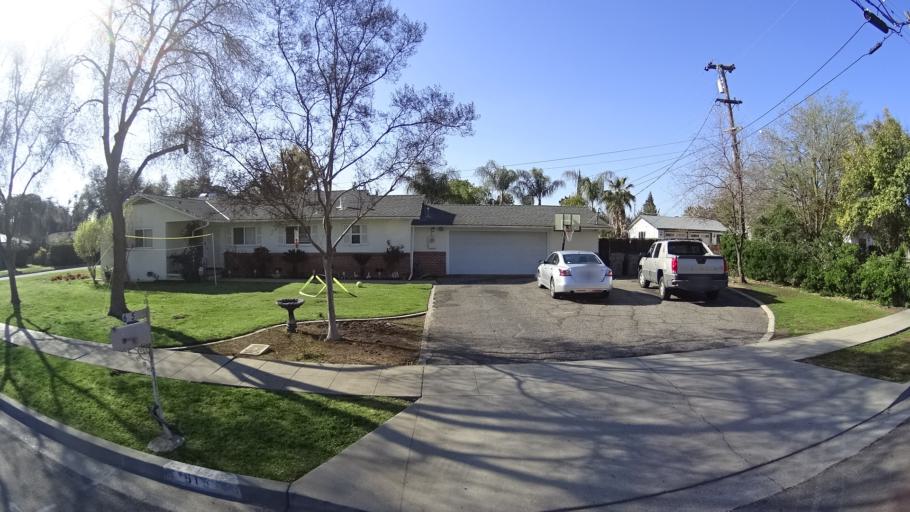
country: US
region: California
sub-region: Fresno County
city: Fresno
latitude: 36.8193
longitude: -119.8044
